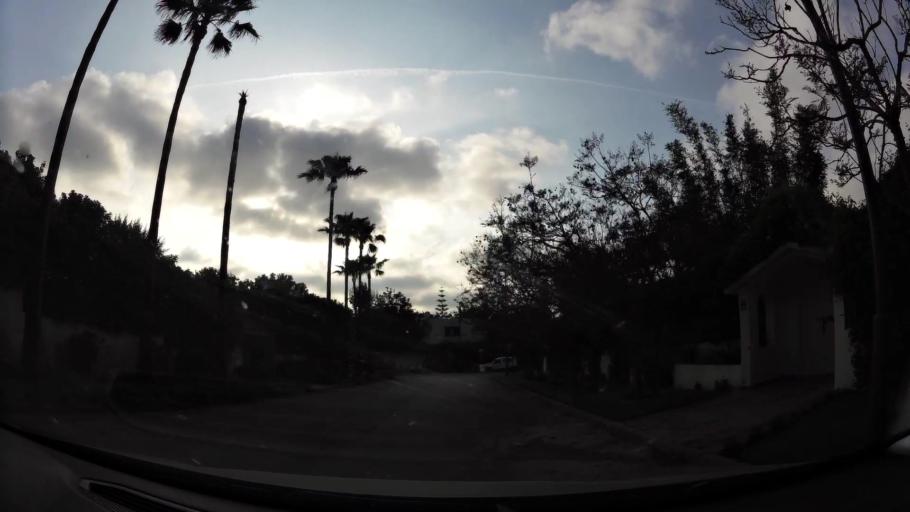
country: MA
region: Rabat-Sale-Zemmour-Zaer
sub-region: Rabat
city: Rabat
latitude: 33.9473
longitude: -6.8170
